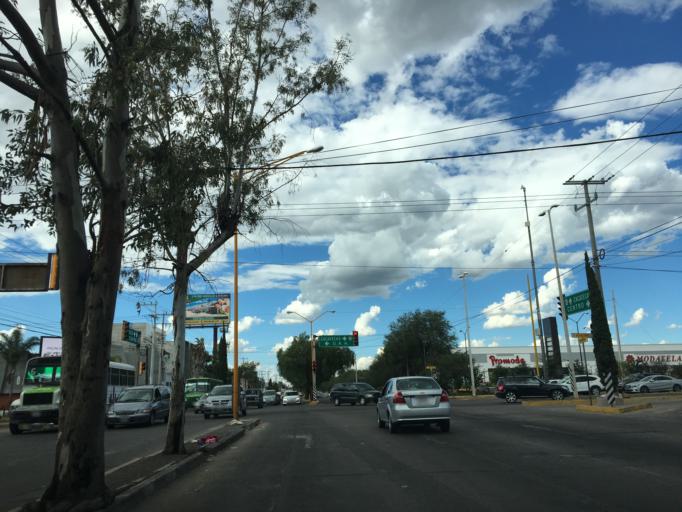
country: MX
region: Aguascalientes
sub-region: Jesus Maria
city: El Llano
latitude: 21.9247
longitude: -102.2980
